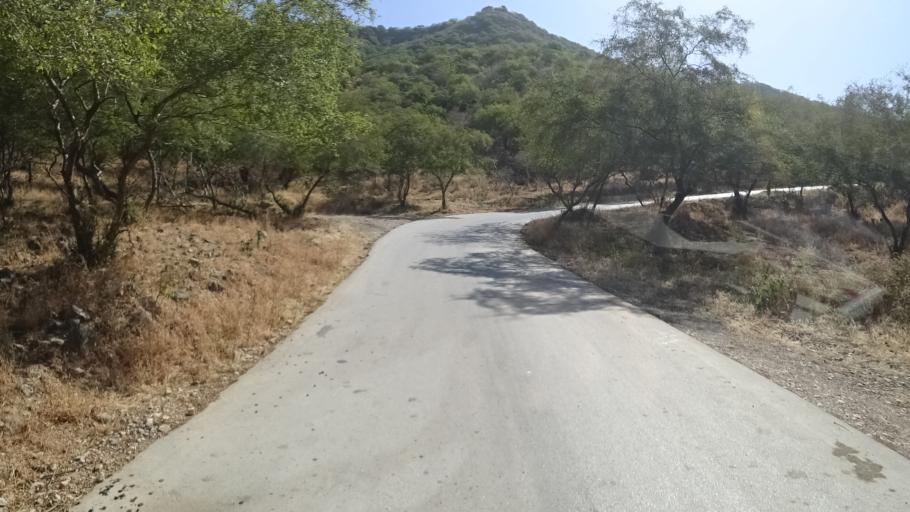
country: OM
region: Zufar
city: Salalah
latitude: 17.0792
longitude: 54.4385
